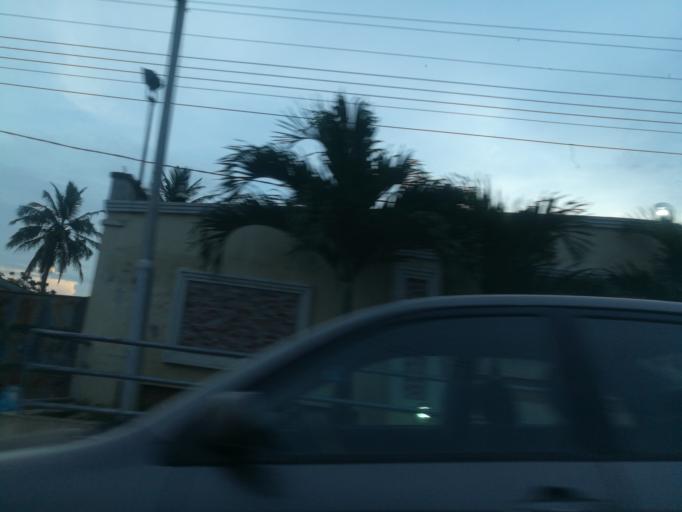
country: NG
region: Oyo
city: Ibadan
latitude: 7.4187
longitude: 3.8982
